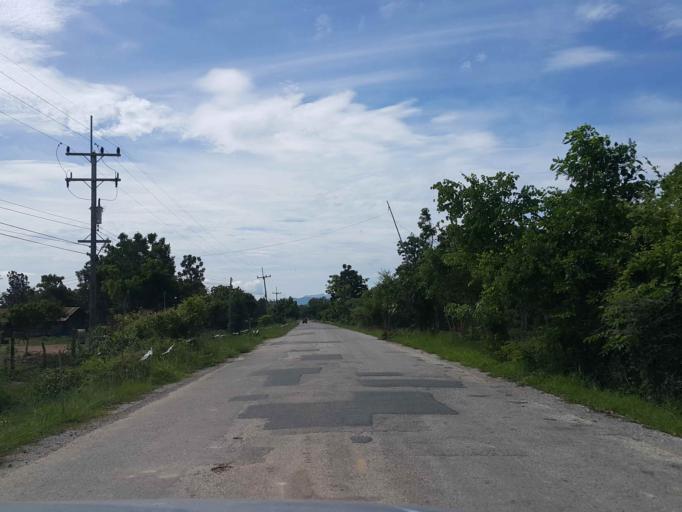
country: TH
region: Sukhothai
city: Ban Dan Lan Hoi
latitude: 17.1238
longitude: 99.5315
